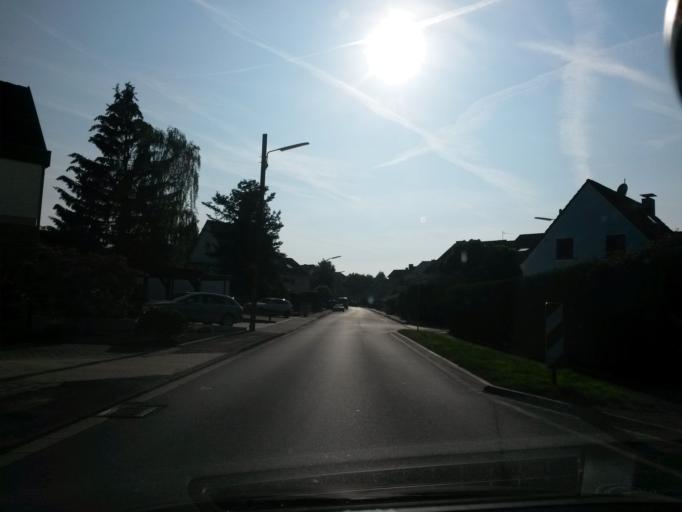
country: DE
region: North Rhine-Westphalia
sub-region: Regierungsbezirk Koln
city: Alfter
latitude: 50.7360
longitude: 7.0181
